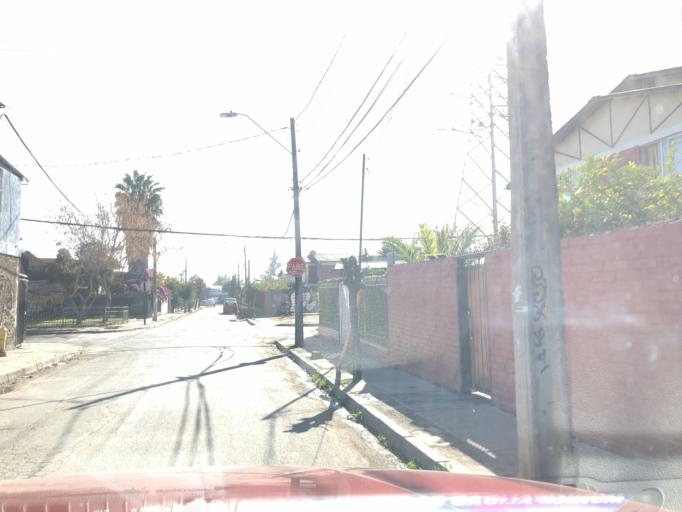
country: CL
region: Santiago Metropolitan
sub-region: Provincia de Cordillera
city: Puente Alto
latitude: -33.5688
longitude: -70.5650
